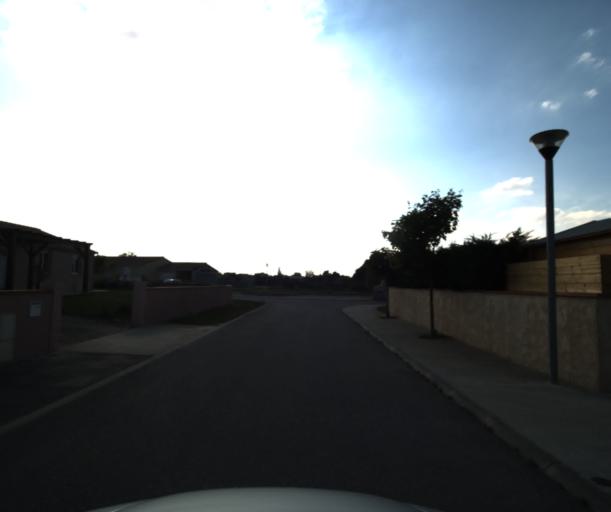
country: FR
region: Midi-Pyrenees
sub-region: Departement de la Haute-Garonne
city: Saint-Lys
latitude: 43.5060
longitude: 1.1949
